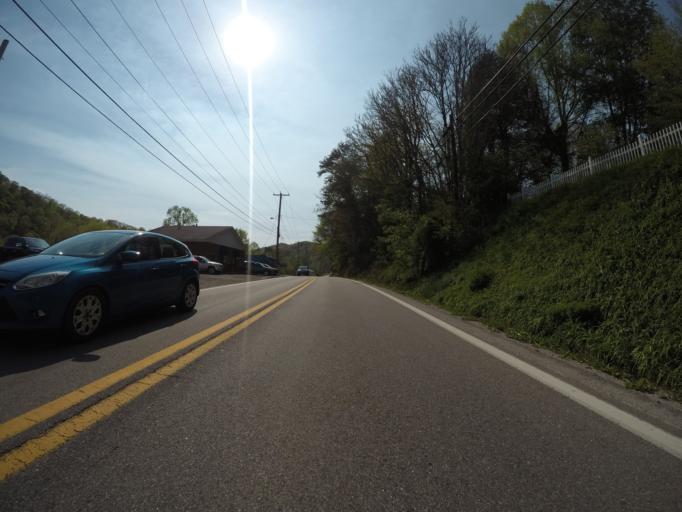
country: US
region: West Virginia
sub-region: Kanawha County
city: Pinch
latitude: 38.4056
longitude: -81.5351
